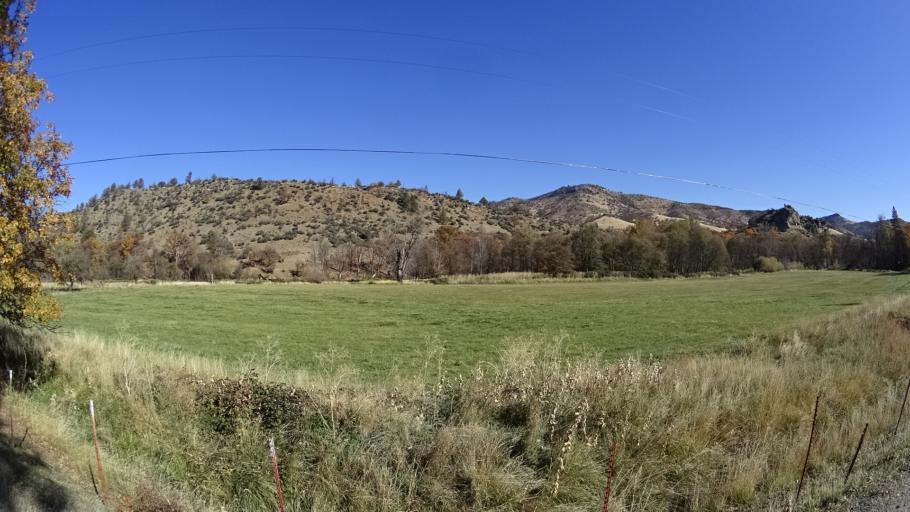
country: US
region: California
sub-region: Siskiyou County
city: Yreka
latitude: 41.9445
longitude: -122.5969
